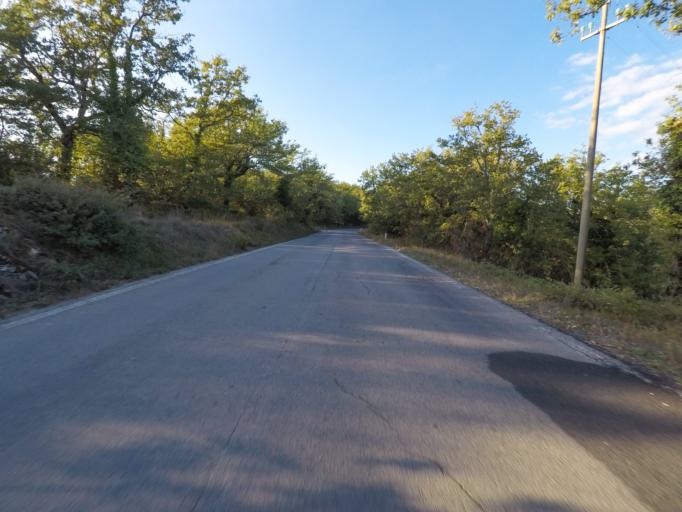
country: IT
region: Tuscany
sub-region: Provincia di Siena
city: Radda in Chianti
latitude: 43.4458
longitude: 11.3944
